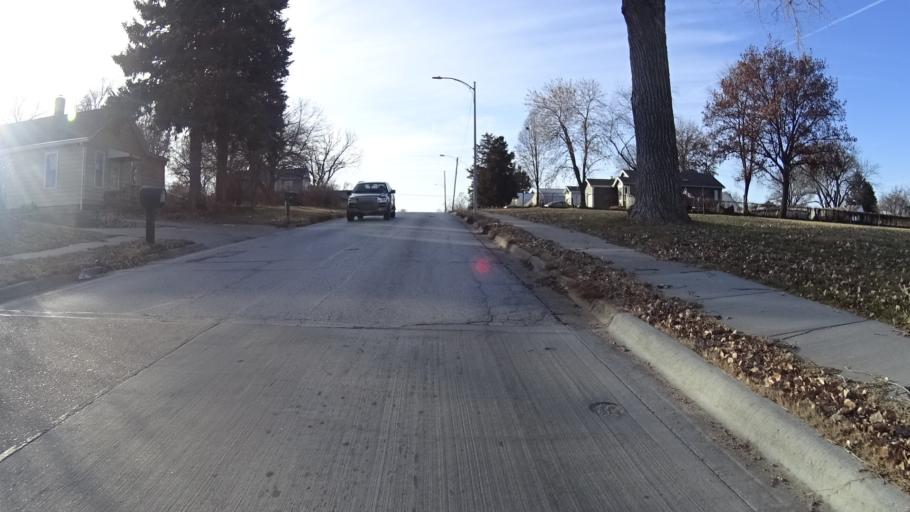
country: US
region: Nebraska
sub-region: Douglas County
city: Omaha
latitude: 41.1909
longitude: -95.9558
